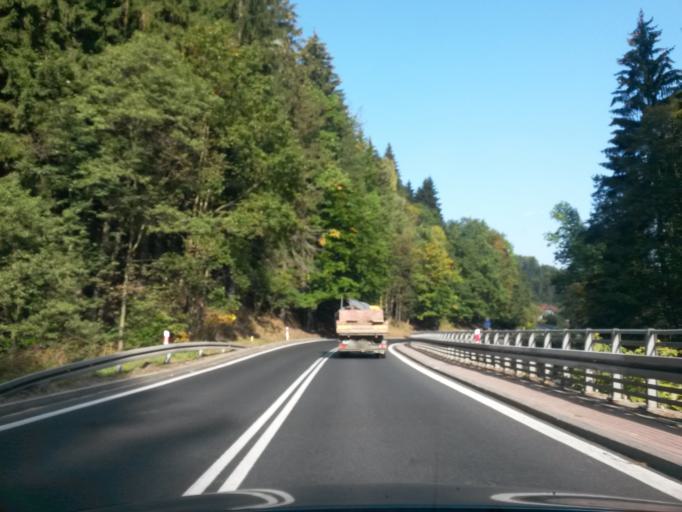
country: PL
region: Lower Silesian Voivodeship
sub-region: Powiat jeleniogorski
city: Piechowice
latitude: 50.8401
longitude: 15.5670
